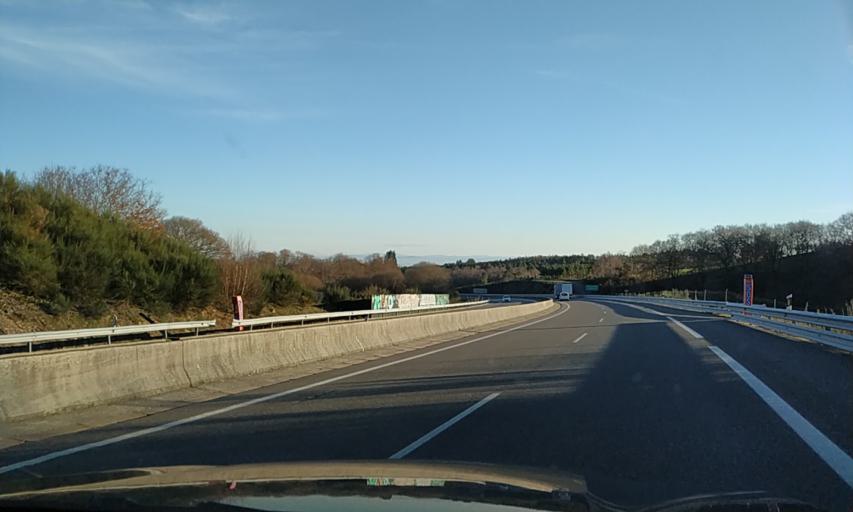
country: ES
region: Galicia
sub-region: Provincia de Pontevedra
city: Dozon
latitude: 42.5444
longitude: -8.0205
